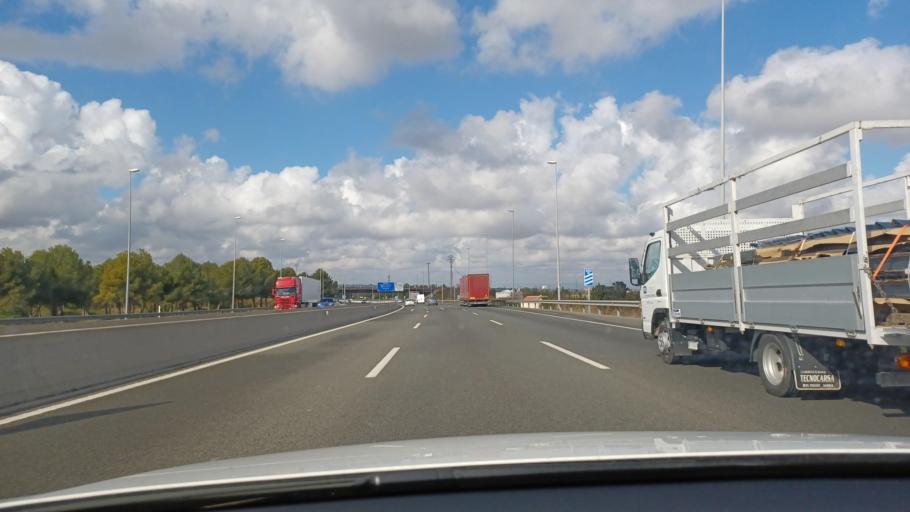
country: ES
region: Valencia
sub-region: Provincia de Valencia
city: Picassent
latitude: 39.3680
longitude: -0.4520
